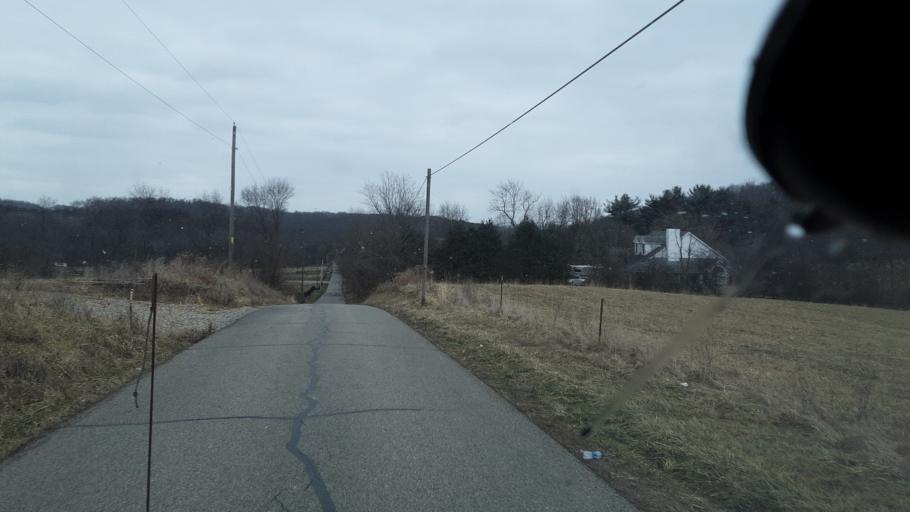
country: US
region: Ohio
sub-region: Perry County
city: Thornport
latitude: 39.9367
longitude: -82.4066
